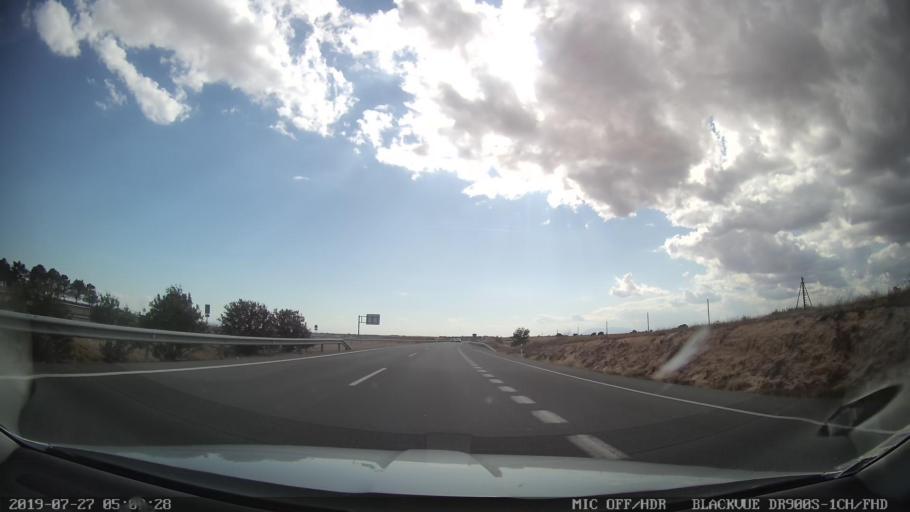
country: ES
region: Castille-La Mancha
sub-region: Province of Toledo
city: Santa Cruz del Retamar
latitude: 40.1188
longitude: -4.2658
